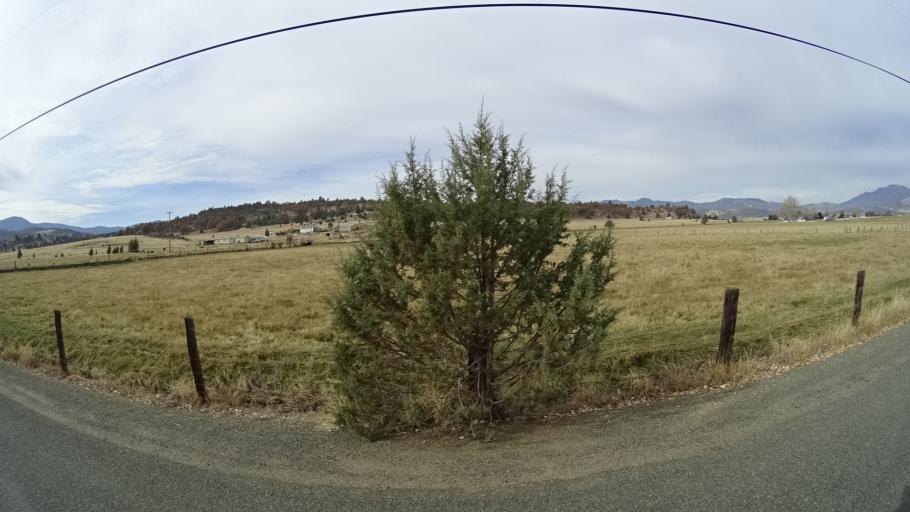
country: US
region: California
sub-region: Siskiyou County
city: Montague
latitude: 41.7025
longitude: -122.5639
